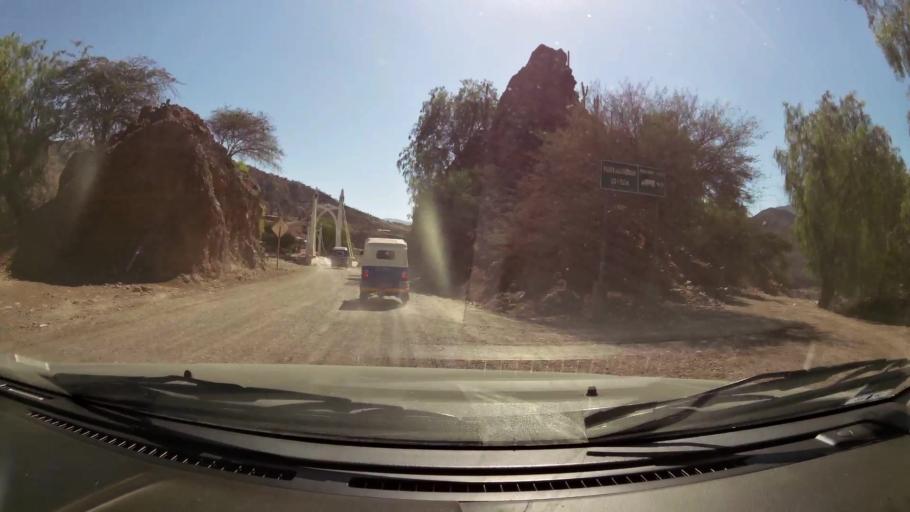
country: PE
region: Ayacucho
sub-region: Provincia de Huanta
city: Luricocha
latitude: -12.8449
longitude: -74.3308
